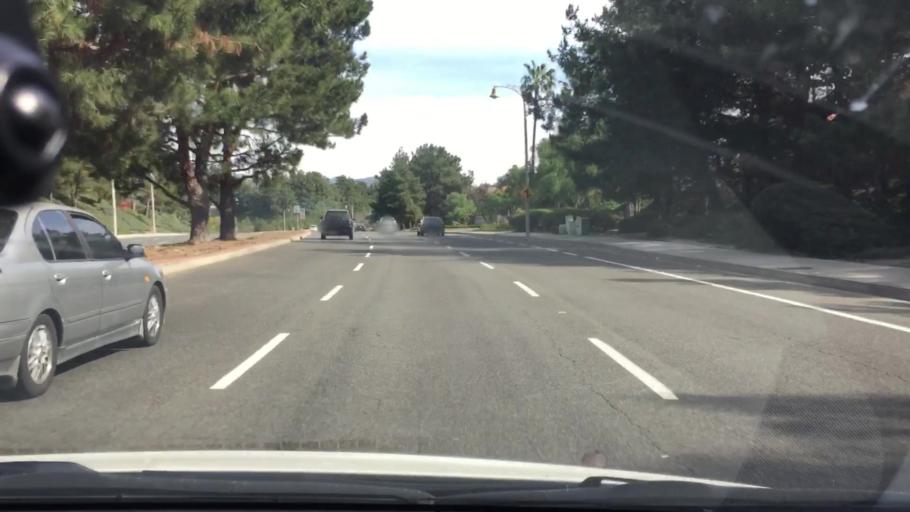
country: US
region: California
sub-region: Orange County
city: Portola Hills
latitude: 33.6509
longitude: -117.6422
